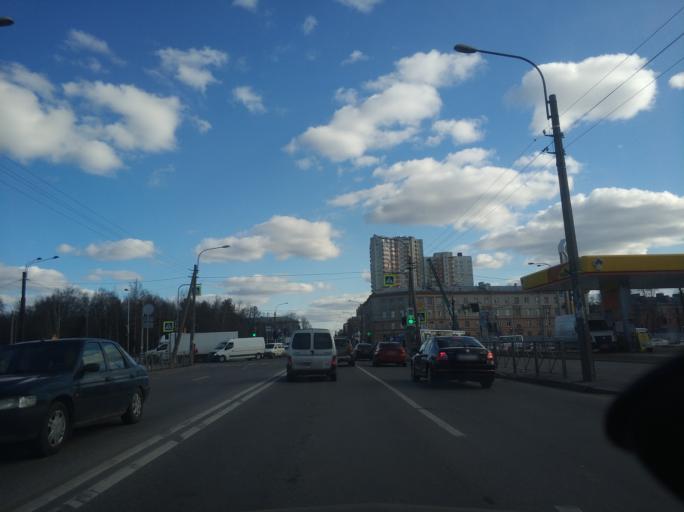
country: RU
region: St.-Petersburg
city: Krasnogvargeisky
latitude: 59.9625
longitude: 30.4880
